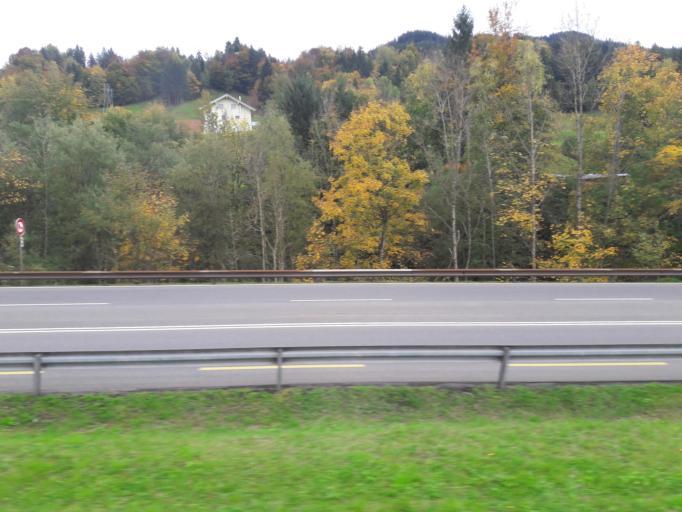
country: CH
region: Schwyz
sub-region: Bezirk Schwyz
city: Rothenthurm
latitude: 47.0890
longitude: 8.6650
